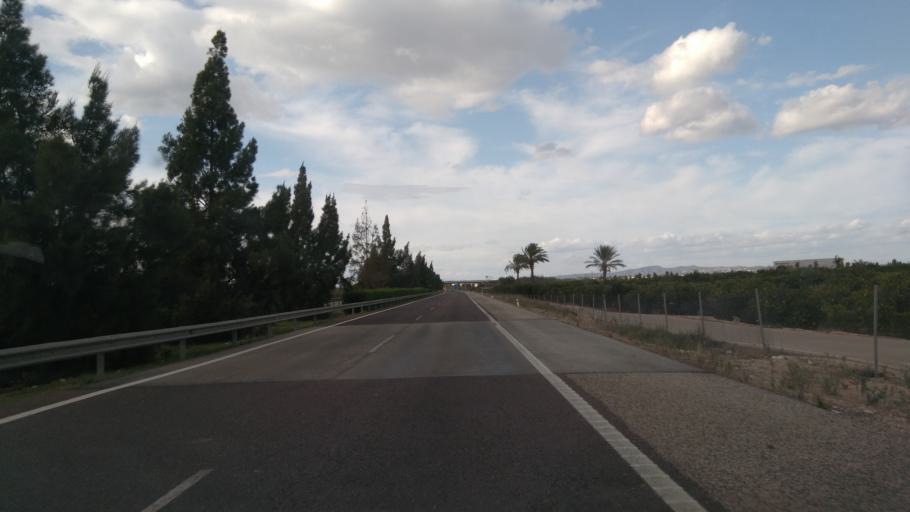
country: ES
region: Valencia
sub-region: Provincia de Valencia
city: Guadassuar
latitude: 39.1664
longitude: -0.4600
